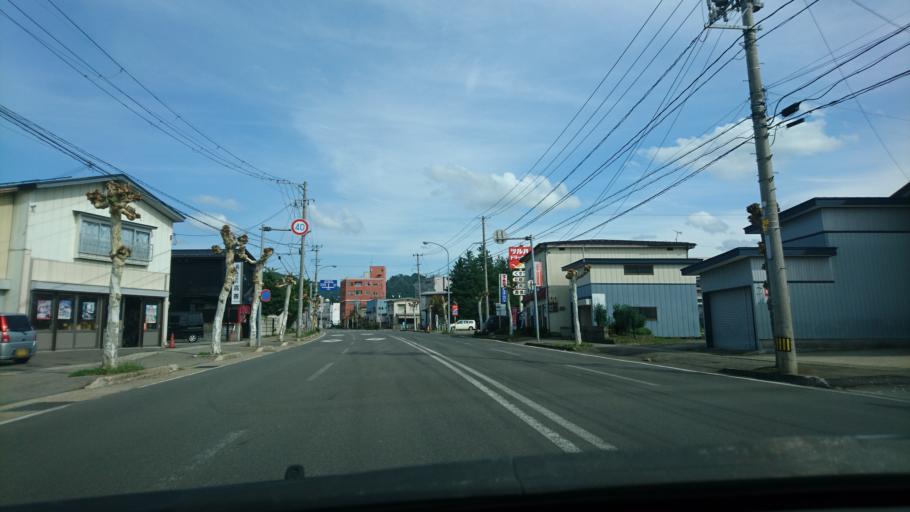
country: JP
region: Akita
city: Yokotemachi
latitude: 39.3091
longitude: 140.5703
